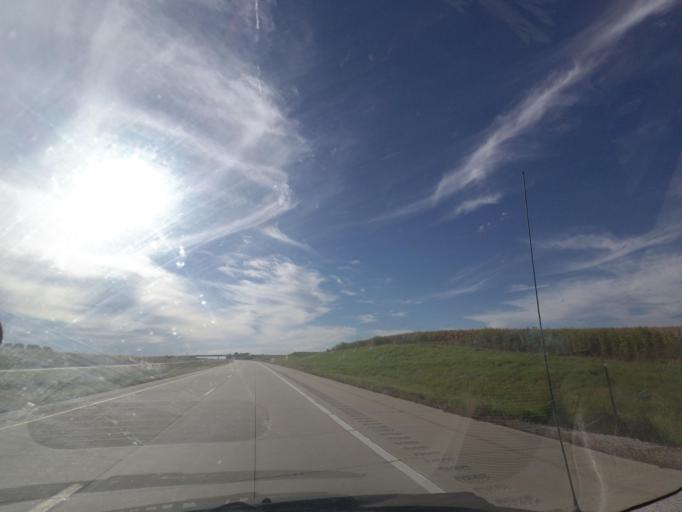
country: US
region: Illinois
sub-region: Sangamon County
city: Riverton
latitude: 39.8396
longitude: -89.4573
